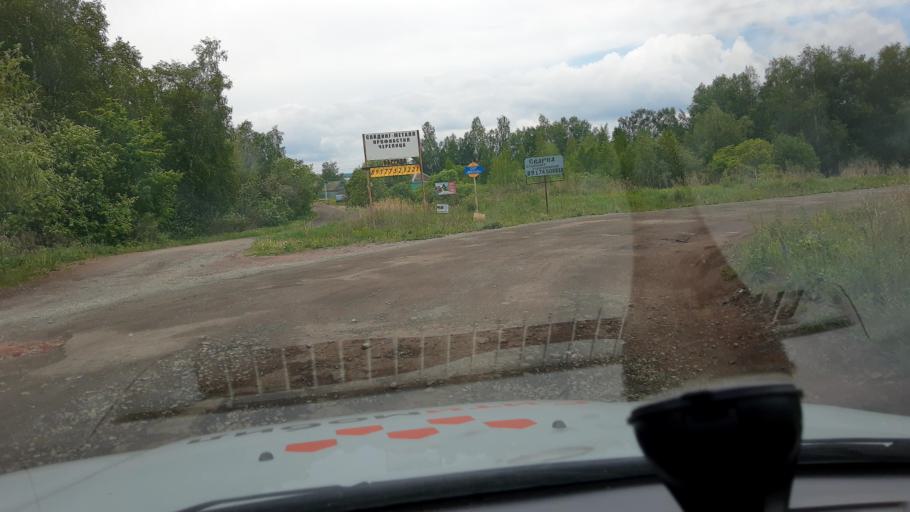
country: RU
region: Bashkortostan
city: Avdon
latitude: 54.6542
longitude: 55.6553
